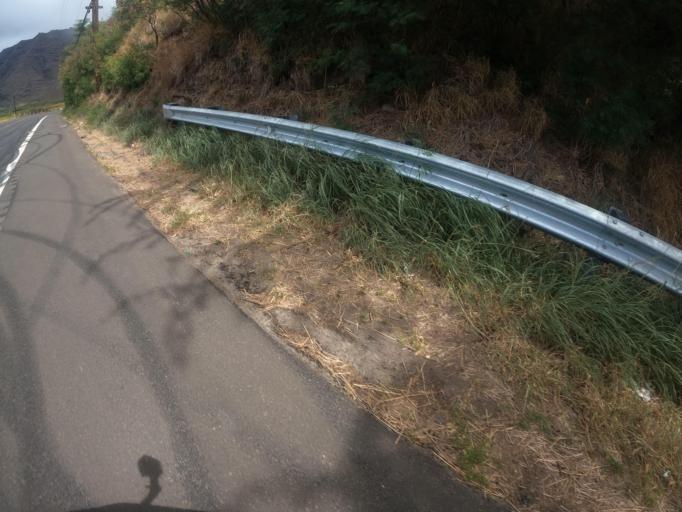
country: US
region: Hawaii
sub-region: Honolulu County
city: Makaha Valley
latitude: 21.5198
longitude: -158.2278
